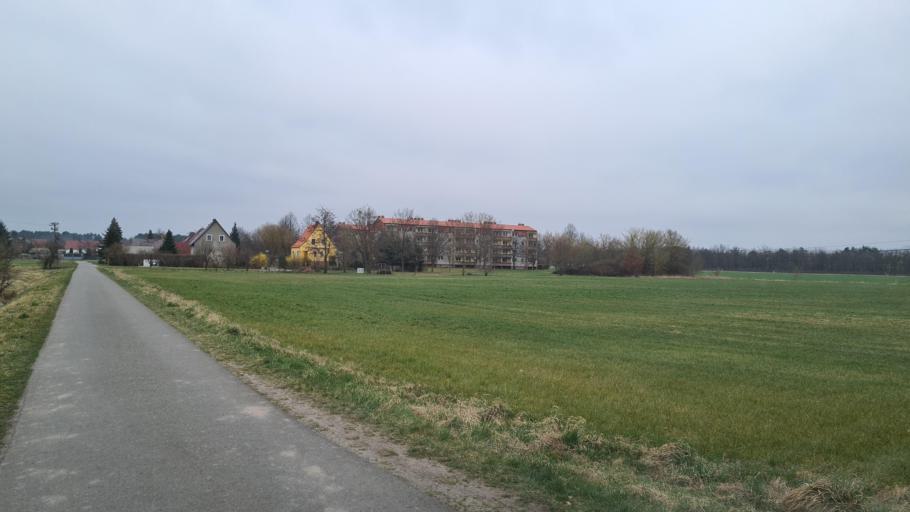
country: DE
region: Brandenburg
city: Finsterwalde
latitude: 51.5966
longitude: 13.7729
